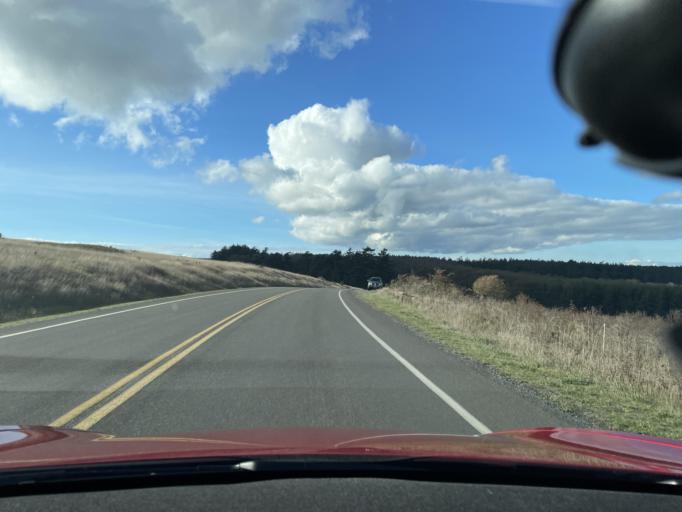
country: US
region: Washington
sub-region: San Juan County
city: Friday Harbor
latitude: 48.4641
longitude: -123.0031
